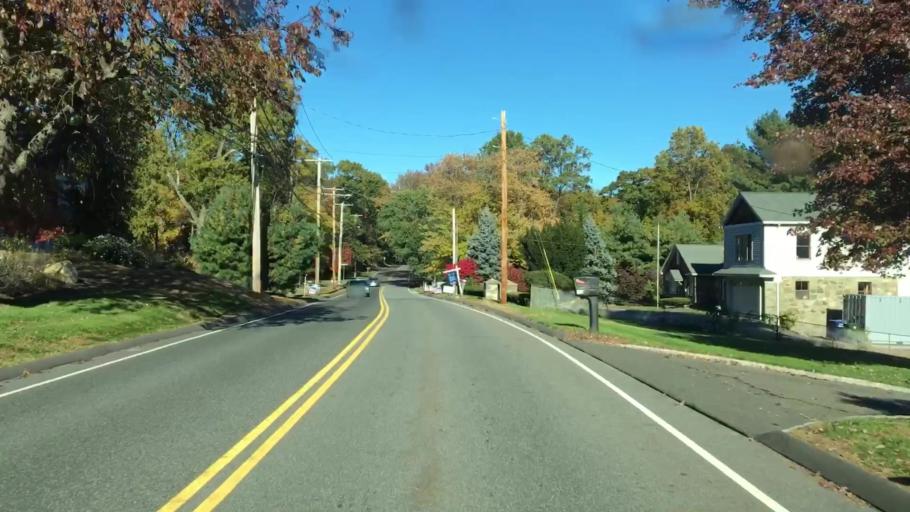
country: US
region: Connecticut
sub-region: Fairfield County
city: Trumbull
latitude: 41.2535
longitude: -73.1505
